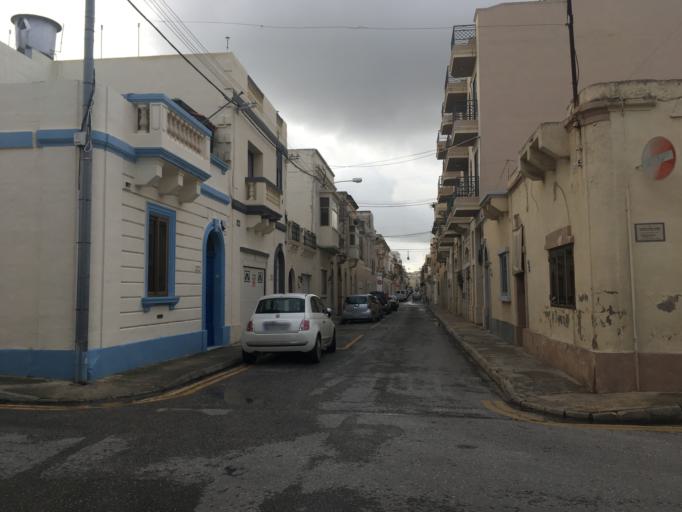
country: MT
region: Il-Mosta
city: Mosta
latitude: 35.9081
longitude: 14.4295
